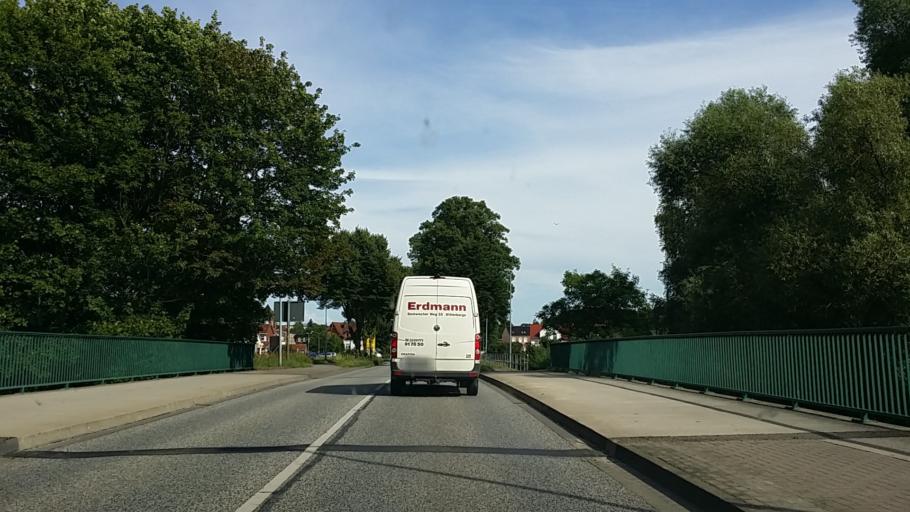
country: DE
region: Brandenburg
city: Perleberg
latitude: 53.0708
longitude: 11.8552
